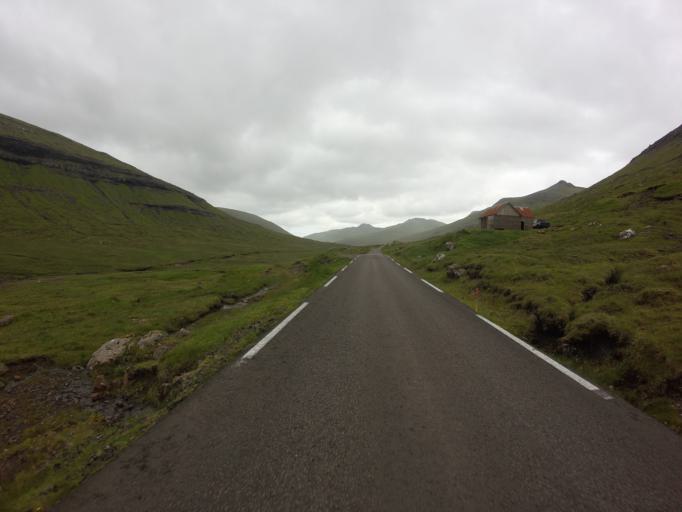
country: FO
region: Streymoy
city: Vestmanna
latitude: 62.2169
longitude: -7.1201
